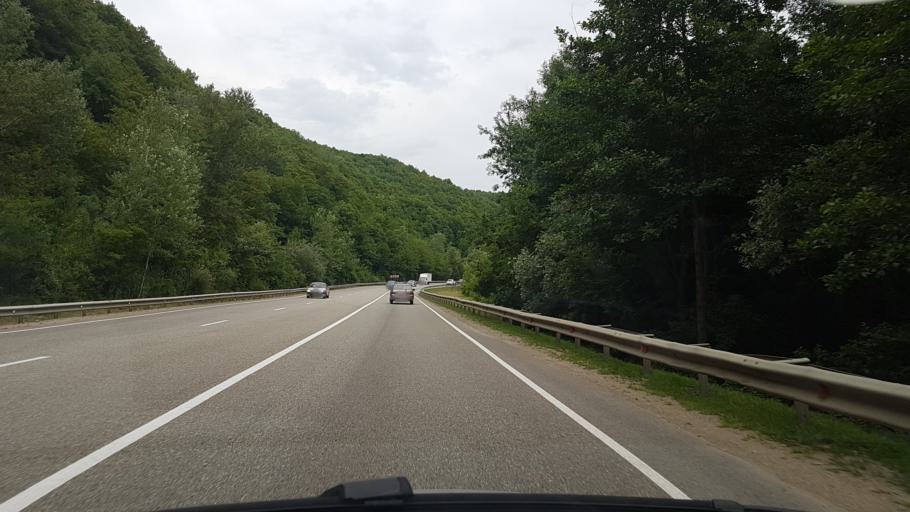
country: RU
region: Krasnodarskiy
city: Goryachiy Klyuch
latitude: 44.5699
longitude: 39.0024
